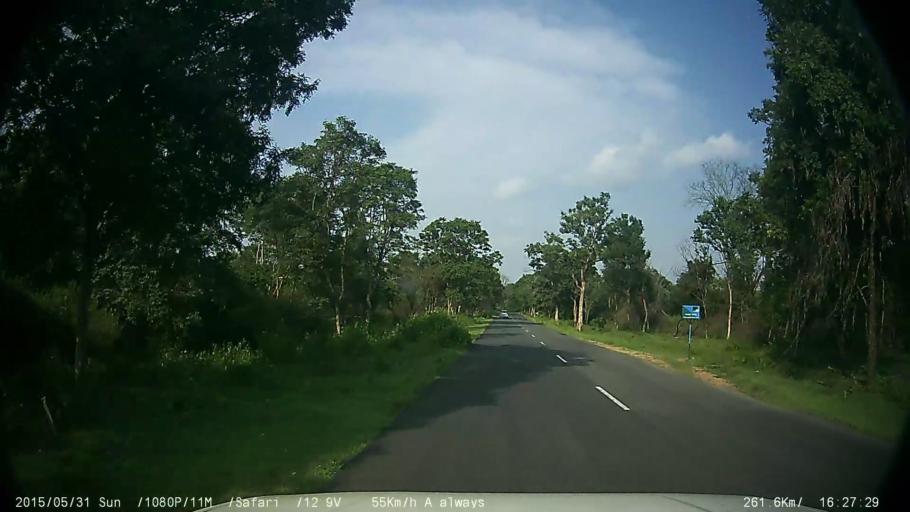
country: IN
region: Karnataka
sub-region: Chamrajnagar
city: Gundlupet
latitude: 11.7673
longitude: 76.5355
